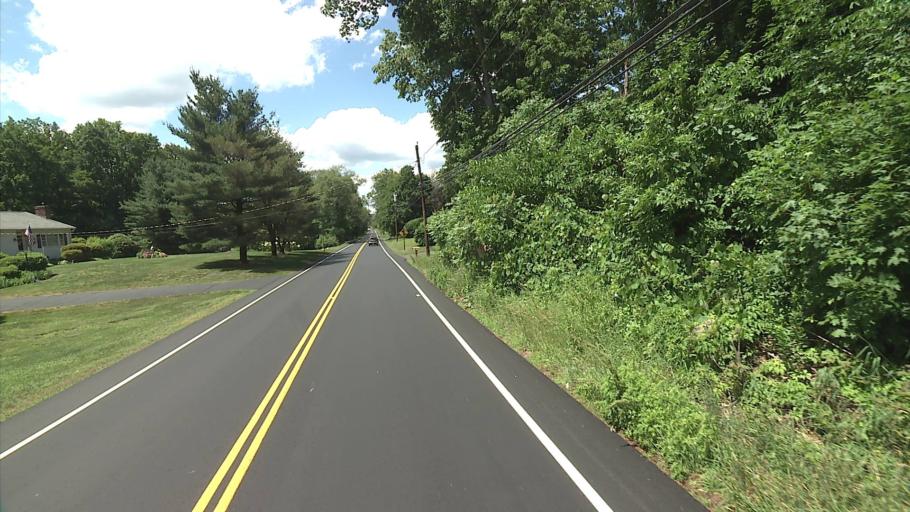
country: US
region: Connecticut
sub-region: Tolland County
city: Somers
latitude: 41.9987
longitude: -72.4324
